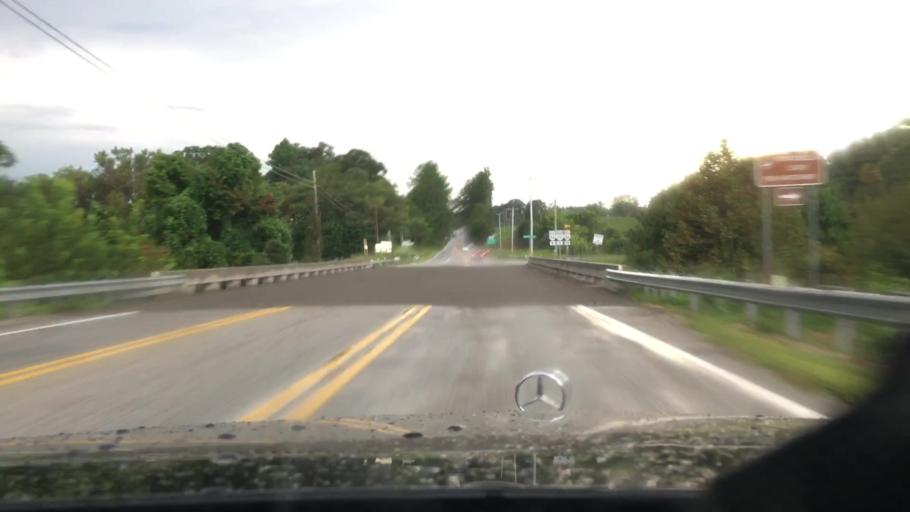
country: US
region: Virginia
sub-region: Nelson County
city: Lovingston
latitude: 37.7539
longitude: -78.9860
